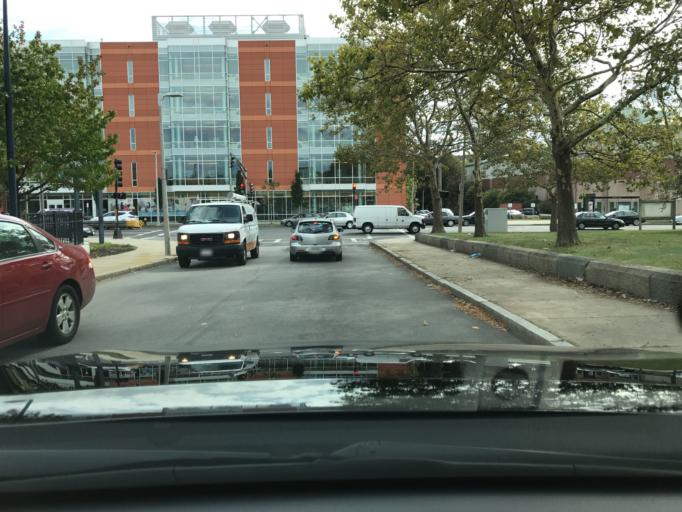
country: US
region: Massachusetts
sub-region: Norfolk County
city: Brookline
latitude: 42.3333
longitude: -71.0927
